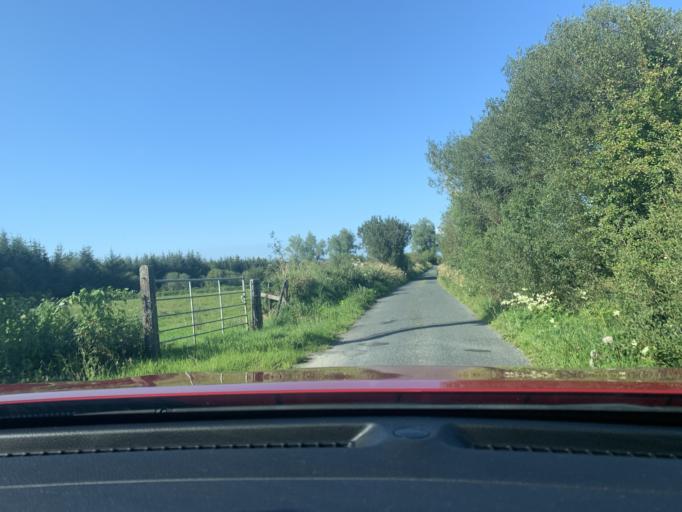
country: IE
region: Connaught
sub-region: Sligo
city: Tobercurry
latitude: 54.0646
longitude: -8.7815
